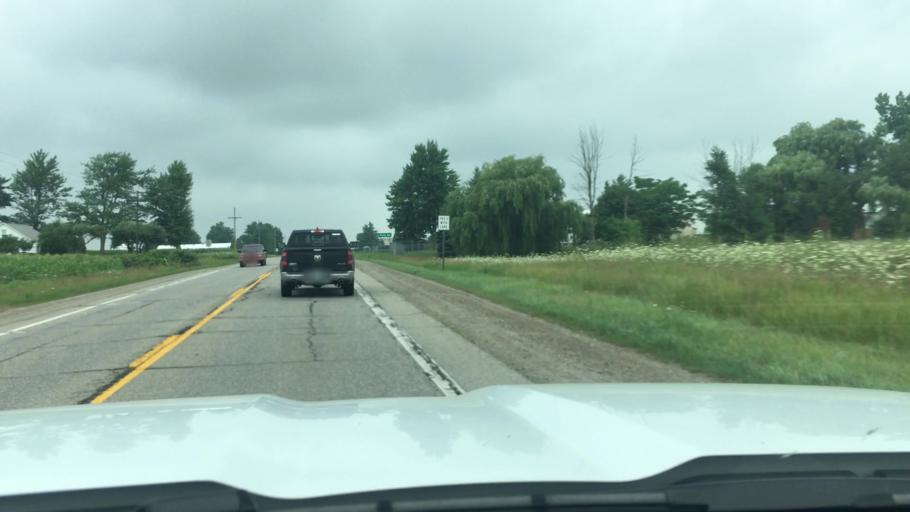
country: US
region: Michigan
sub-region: Sanilac County
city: Marlette
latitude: 43.2523
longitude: -83.0793
